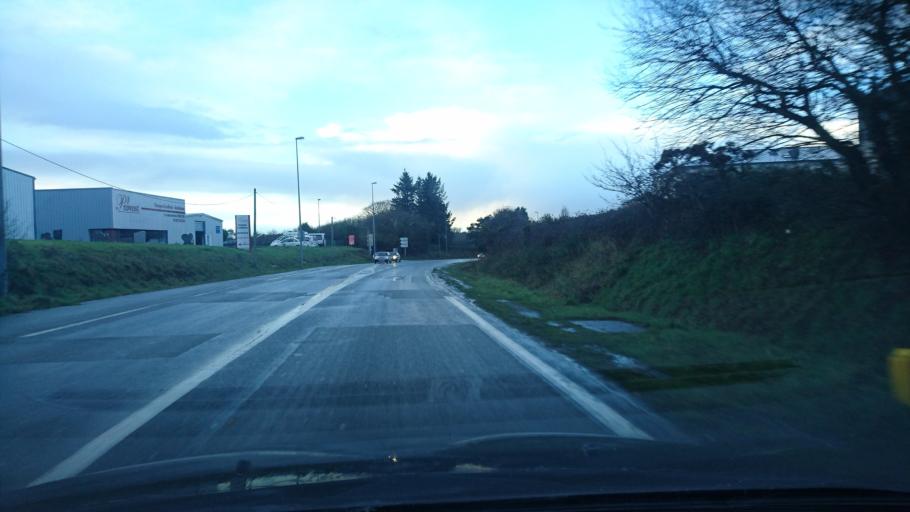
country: FR
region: Brittany
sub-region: Departement du Finistere
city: Guilers
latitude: 48.3923
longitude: -4.5392
